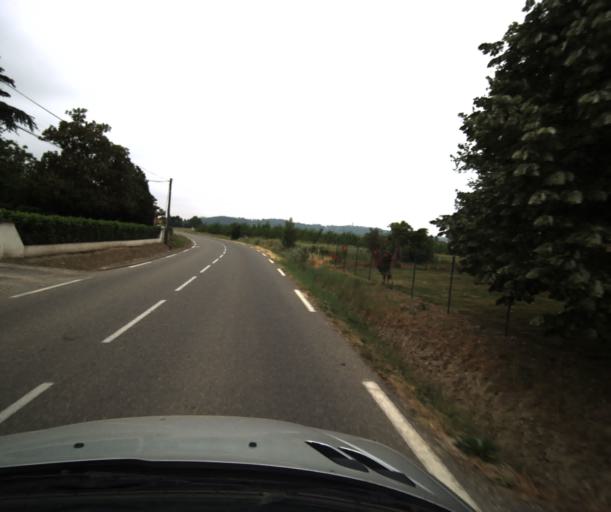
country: FR
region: Midi-Pyrenees
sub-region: Departement du Tarn-et-Garonne
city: Saint-Nicolas-de-la-Grave
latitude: 44.0723
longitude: 1.0037
